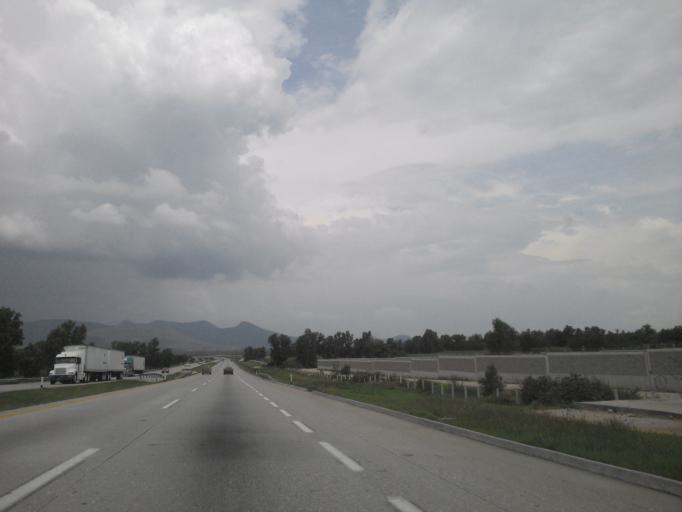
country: MX
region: Hidalgo
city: Doxey
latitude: 20.0769
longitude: -99.2398
